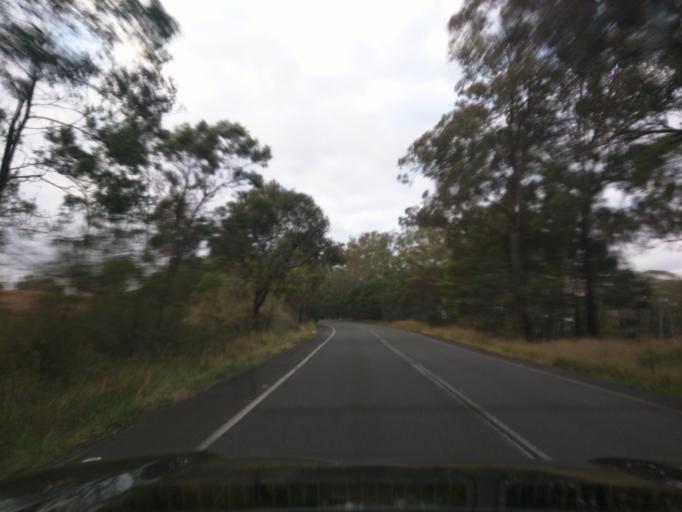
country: AU
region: New South Wales
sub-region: Wollondilly
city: Douglas Park
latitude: -34.2643
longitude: 150.7180
